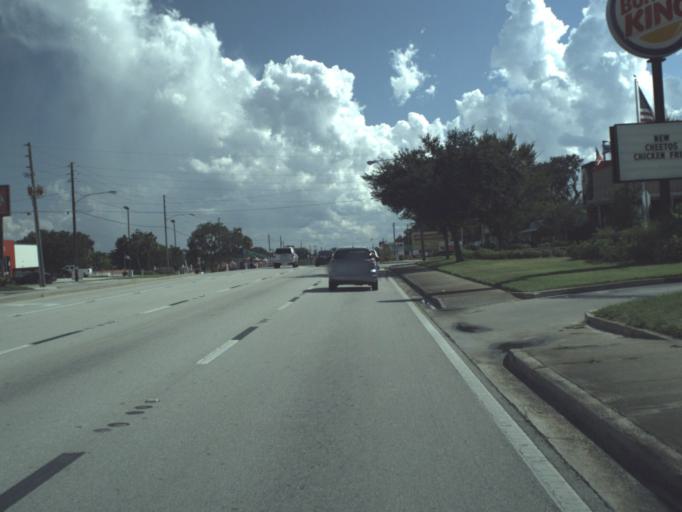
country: US
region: Florida
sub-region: Highlands County
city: Avon Park
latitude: 27.5919
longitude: -81.5146
